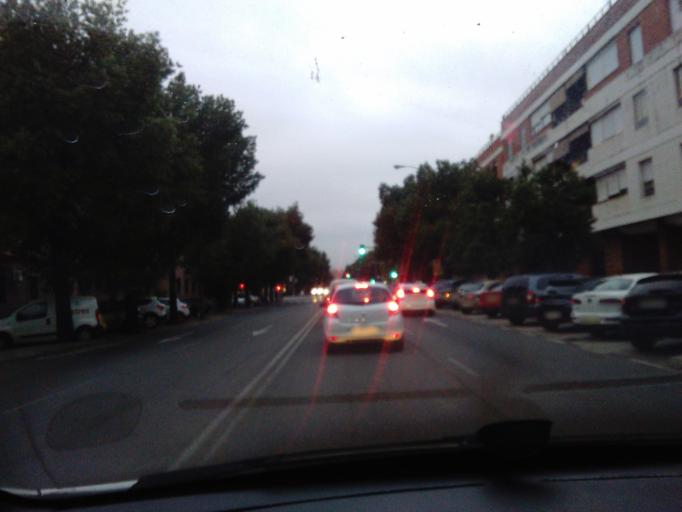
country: ES
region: Andalusia
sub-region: Provincia de Sevilla
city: Sevilla
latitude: 37.3726
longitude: -5.9755
